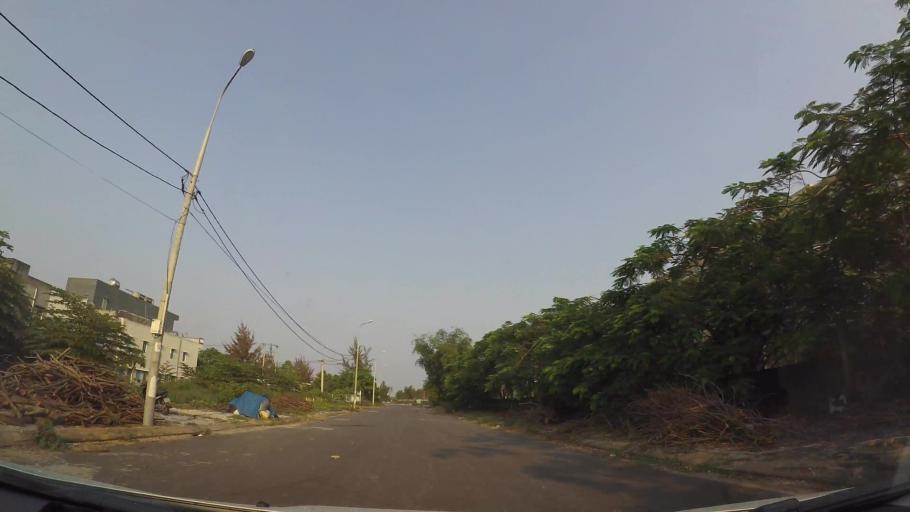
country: VN
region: Da Nang
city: Ngu Hanh Son
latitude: 15.9756
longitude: 108.2560
